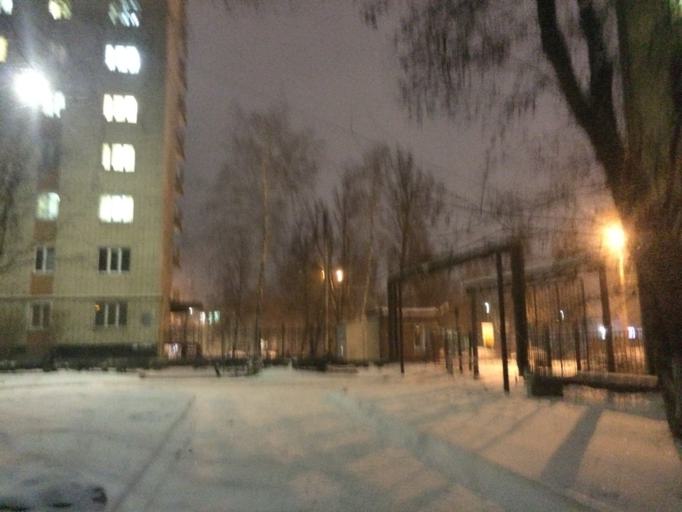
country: RU
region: Tula
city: Tula
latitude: 54.1741
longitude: 37.5919
